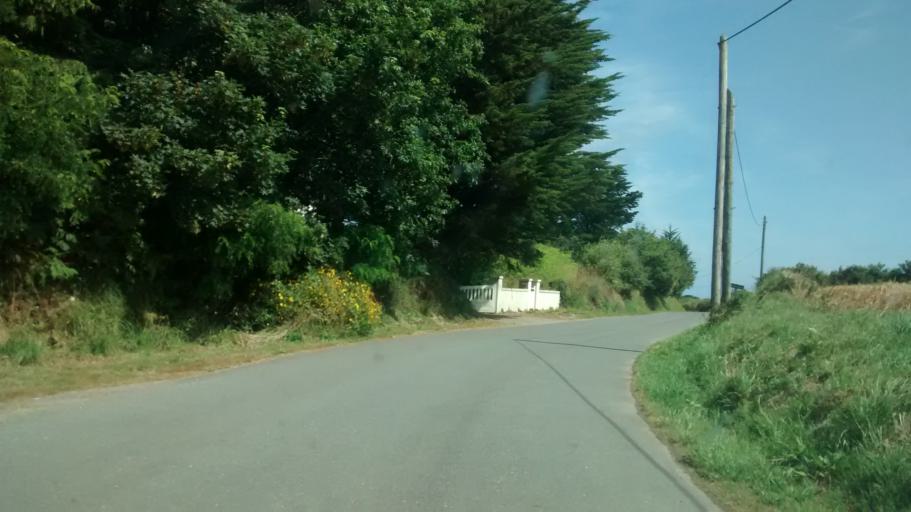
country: FR
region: Brittany
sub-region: Departement du Finistere
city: Plouguerneau
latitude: 48.6160
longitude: -4.4805
